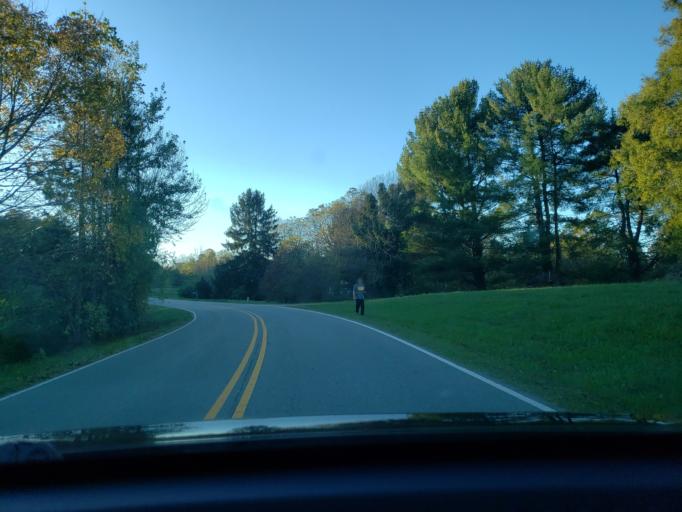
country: US
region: North Carolina
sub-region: Forsyth County
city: Walkertown
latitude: 36.2254
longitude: -80.1973
